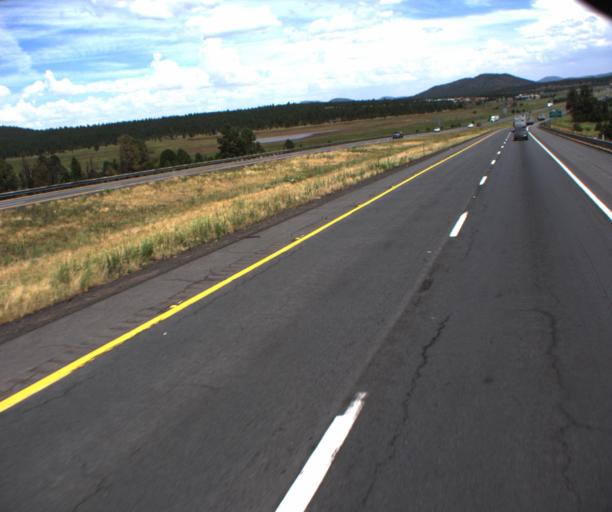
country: US
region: Arizona
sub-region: Coconino County
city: Williams
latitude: 35.2506
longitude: -112.2077
